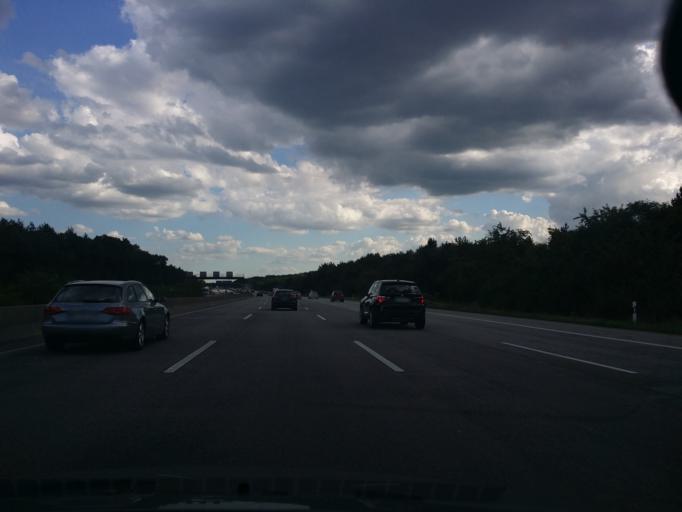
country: DE
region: Hesse
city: Morfelden-Walldorf
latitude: 50.0290
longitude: 8.5931
